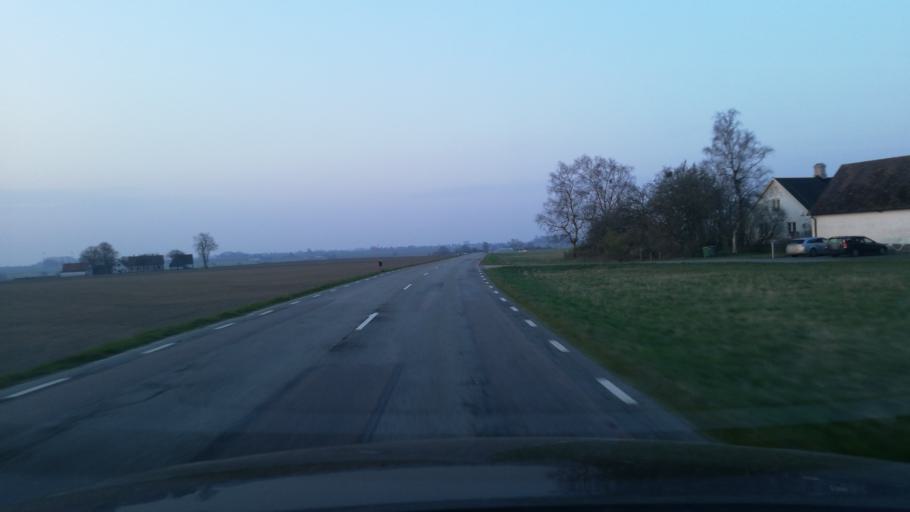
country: SE
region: Skane
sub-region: Tomelilla Kommun
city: Tomelilla
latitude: 55.4877
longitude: 14.1026
